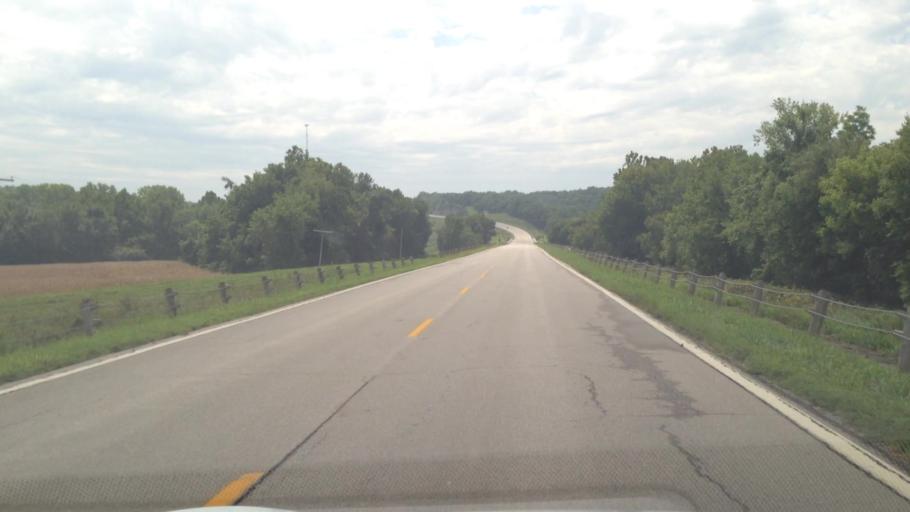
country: US
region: Kansas
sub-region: Bourbon County
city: Fort Scott
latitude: 37.8384
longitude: -94.9814
